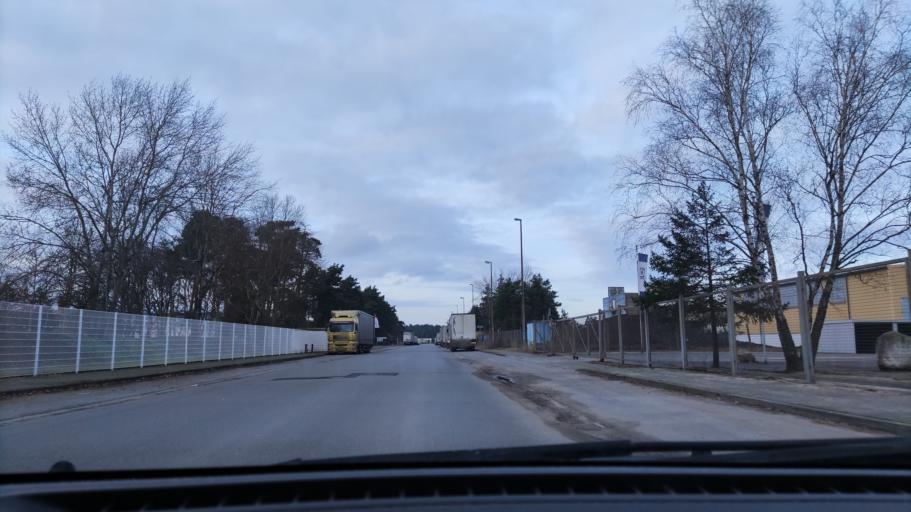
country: DE
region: Lower Saxony
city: Wendisch Evern
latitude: 53.2414
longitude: 10.4785
